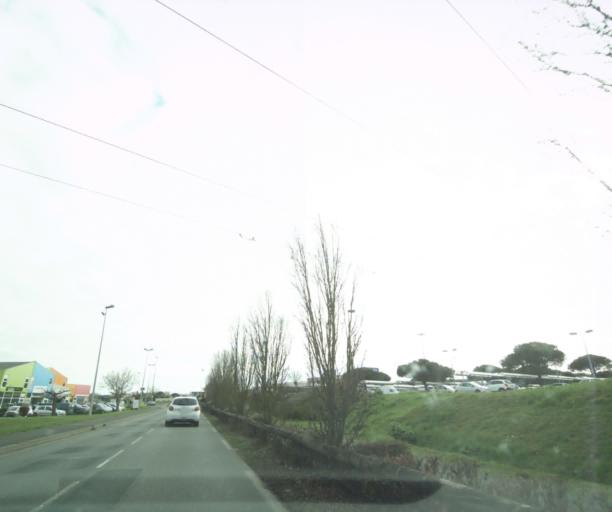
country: FR
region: Poitou-Charentes
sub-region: Departement de la Charente-Maritime
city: Lagord
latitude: 46.1755
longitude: -1.1670
